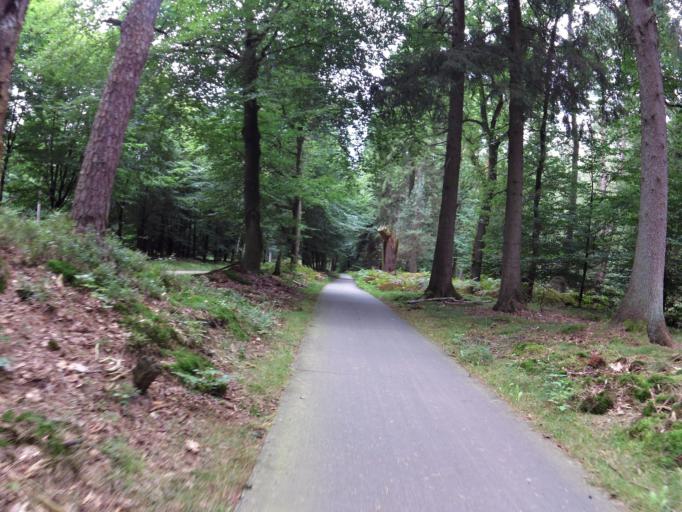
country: NL
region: Gelderland
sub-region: Gemeente Rheden
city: De Steeg
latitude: 52.0488
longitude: 6.0615
